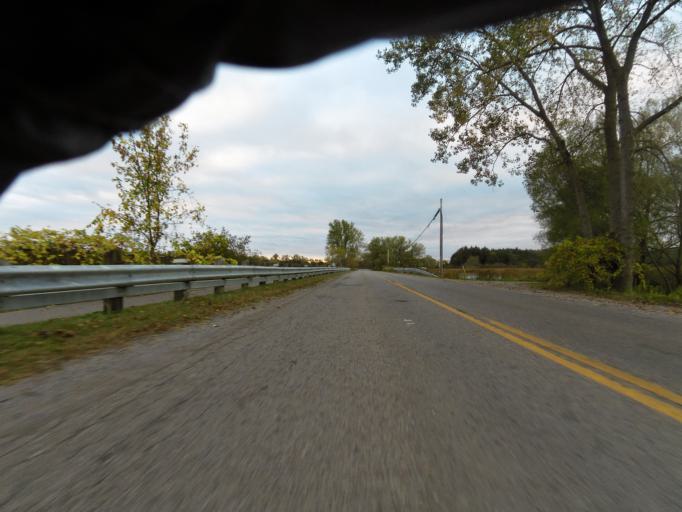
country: CA
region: Ontario
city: Quinte West
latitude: 44.0148
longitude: -77.7377
